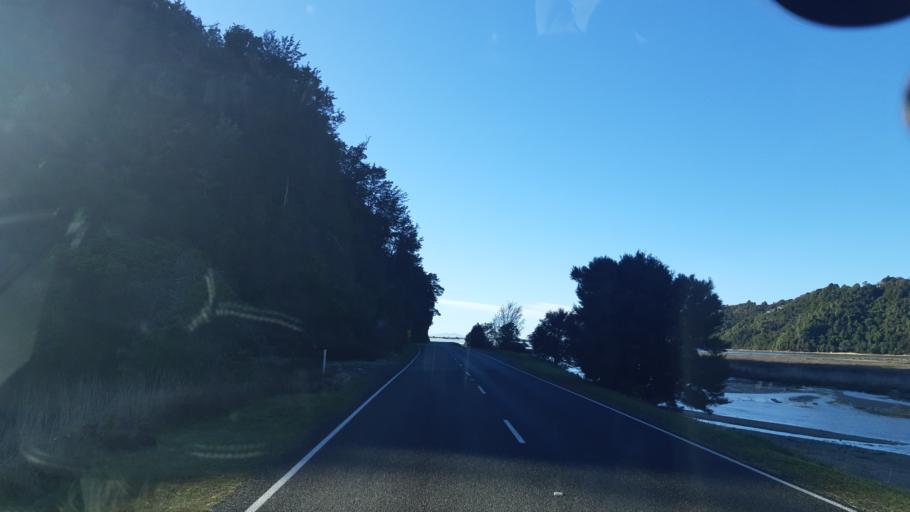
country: NZ
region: Tasman
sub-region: Tasman District
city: Motueka
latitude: -41.0147
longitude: 172.9944
